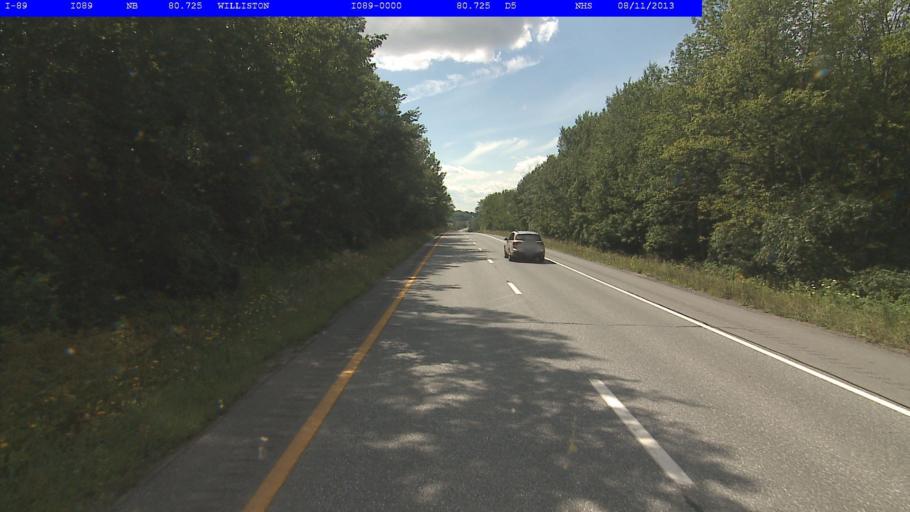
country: US
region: Vermont
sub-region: Chittenden County
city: Williston
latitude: 44.4334
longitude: -73.0503
